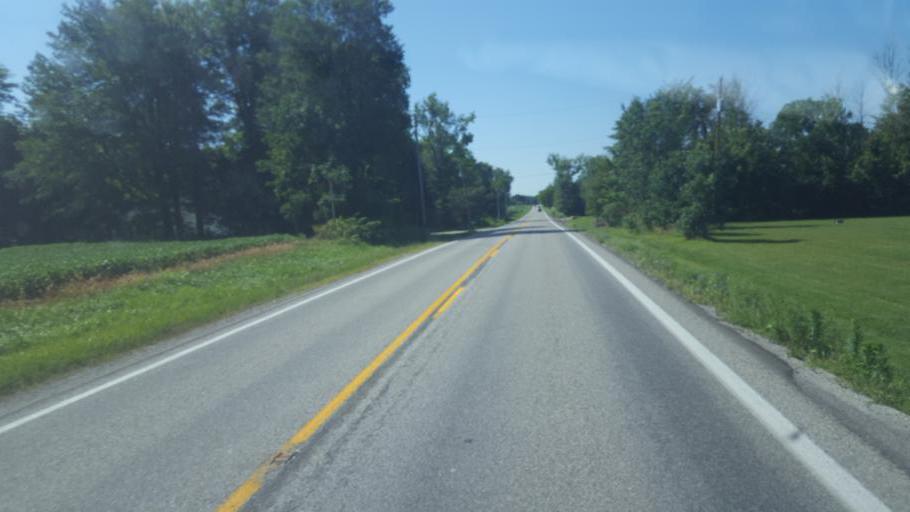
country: US
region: Ohio
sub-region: Morrow County
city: Mount Gilead
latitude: 40.4746
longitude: -82.8211
